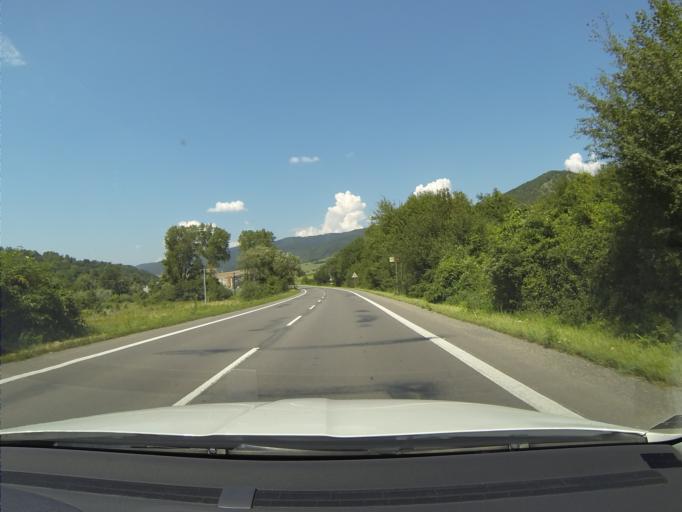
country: SK
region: Nitriansky
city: Handlova
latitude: 48.7564
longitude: 18.7640
